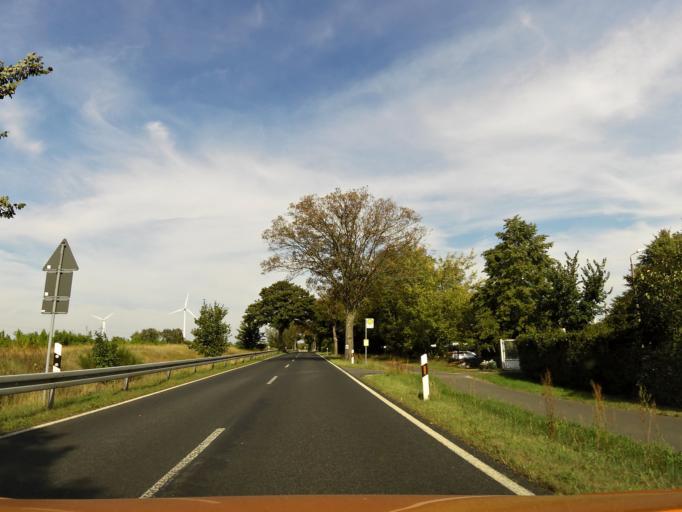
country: DE
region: Brandenburg
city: Ludwigsfelde
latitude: 52.3269
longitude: 13.2498
